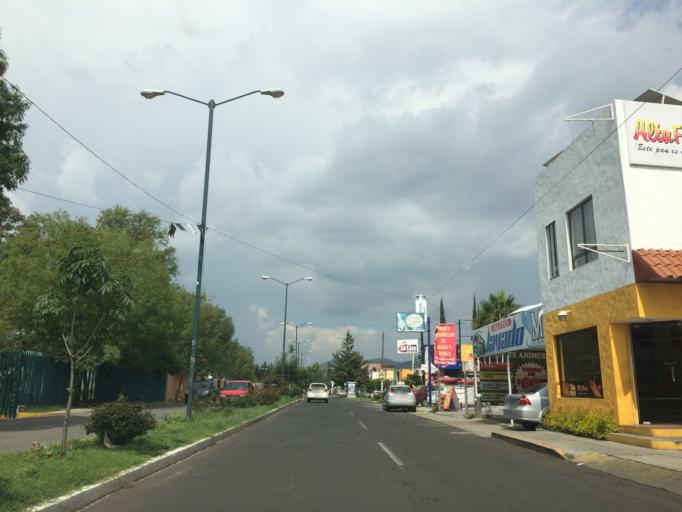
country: MX
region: Michoacan
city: Morelia
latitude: 19.6865
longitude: -101.2067
